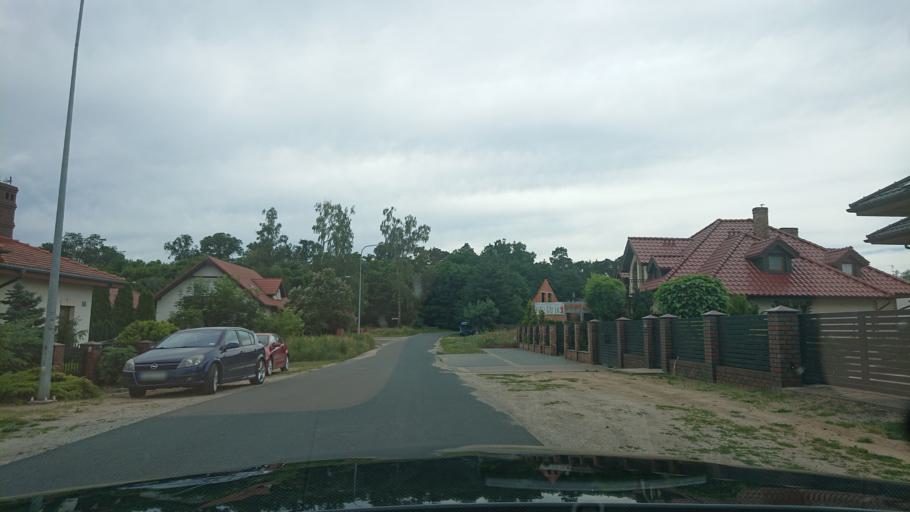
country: PL
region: Greater Poland Voivodeship
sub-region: Powiat gnieznienski
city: Gniezno
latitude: 52.5080
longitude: 17.6108
